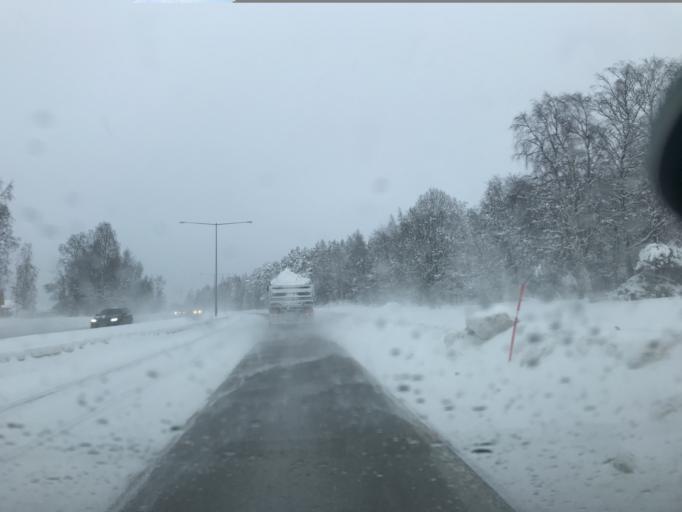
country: SE
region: Norrbotten
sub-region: Lulea Kommun
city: Lulea
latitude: 65.6055
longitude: 22.1383
